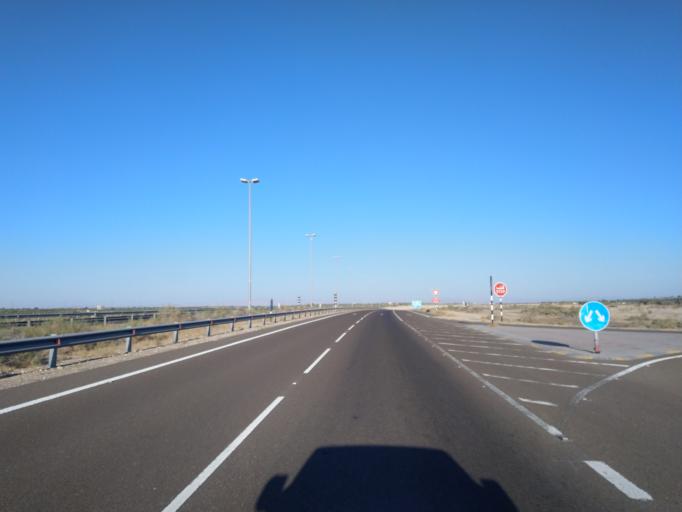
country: OM
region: Al Buraimi
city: Al Buraymi
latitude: 24.5361
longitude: 55.5900
